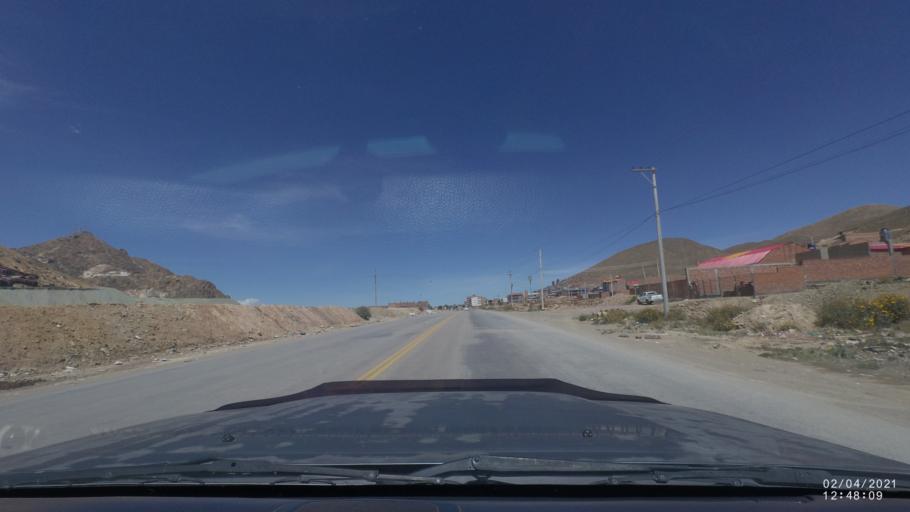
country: BO
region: Oruro
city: Oruro
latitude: -17.9613
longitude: -67.1422
